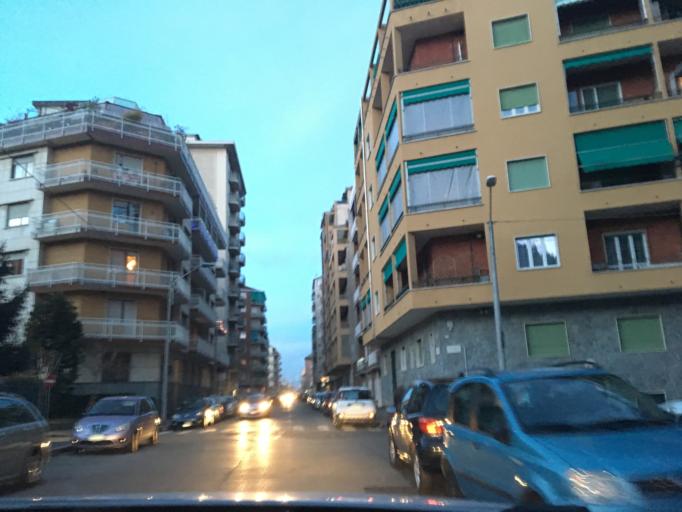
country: IT
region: Piedmont
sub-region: Provincia di Torino
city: Lesna
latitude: 45.0484
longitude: 7.6384
